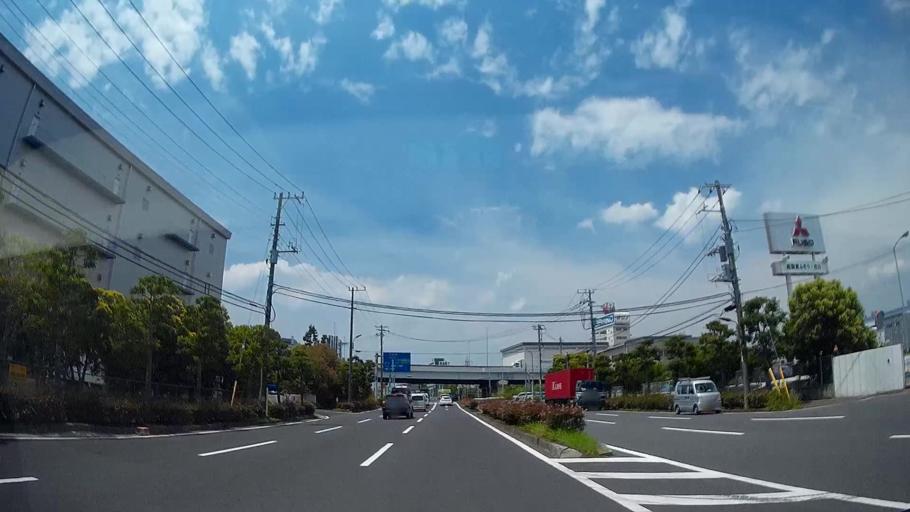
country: JP
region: Tokyo
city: Urayasu
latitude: 35.6599
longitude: 139.9171
